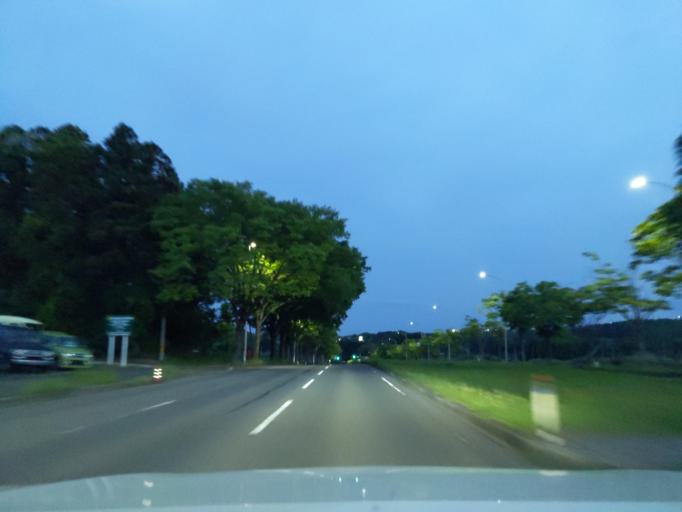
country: JP
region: Miyagi
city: Sendai-shi
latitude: 38.3326
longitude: 140.8403
